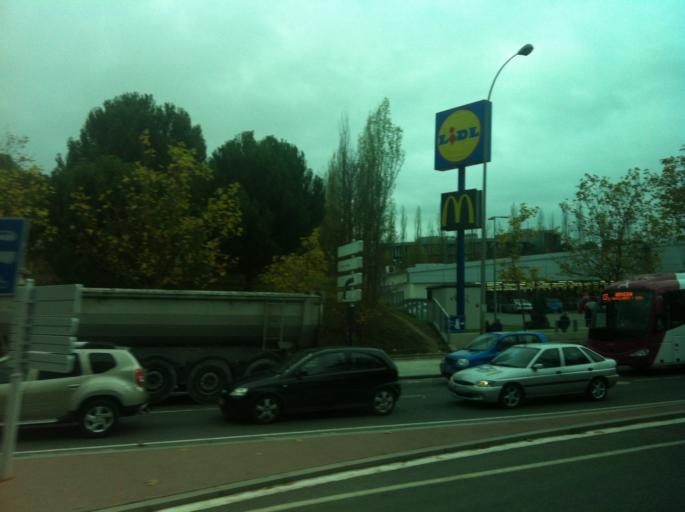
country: ES
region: Basque Country
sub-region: Provincia de Alava
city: Gasteiz / Vitoria
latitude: 42.8377
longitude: -2.6974
